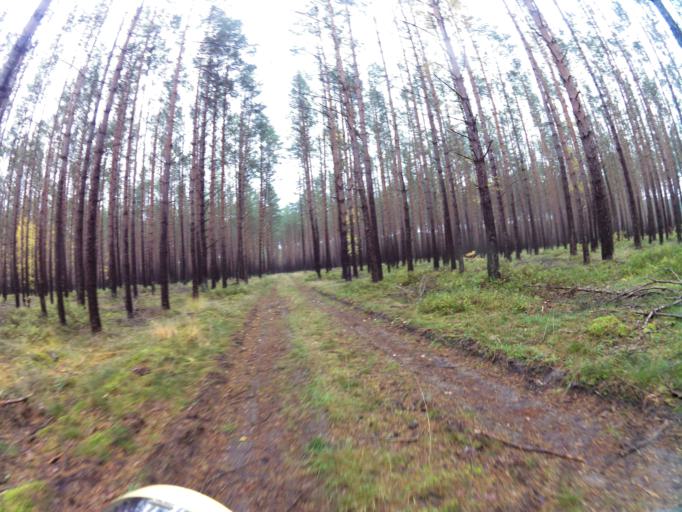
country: PL
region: West Pomeranian Voivodeship
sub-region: Powiat policki
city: Dobra
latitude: 53.6045
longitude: 14.3403
